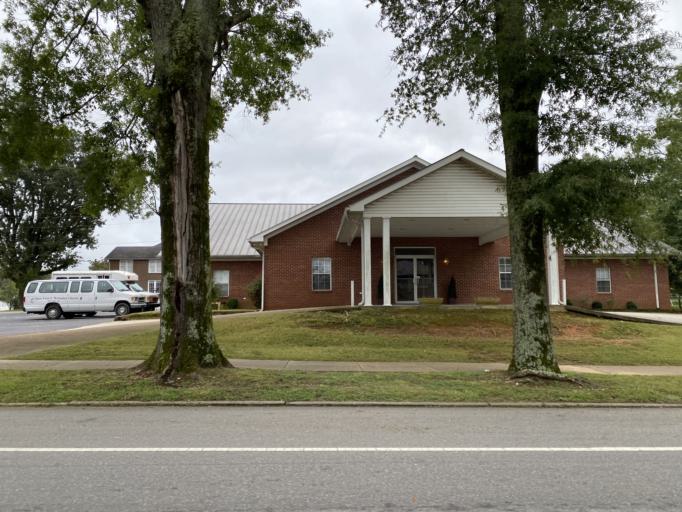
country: US
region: Alabama
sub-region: Franklin County
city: Red Bay
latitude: 34.4426
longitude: -88.1479
